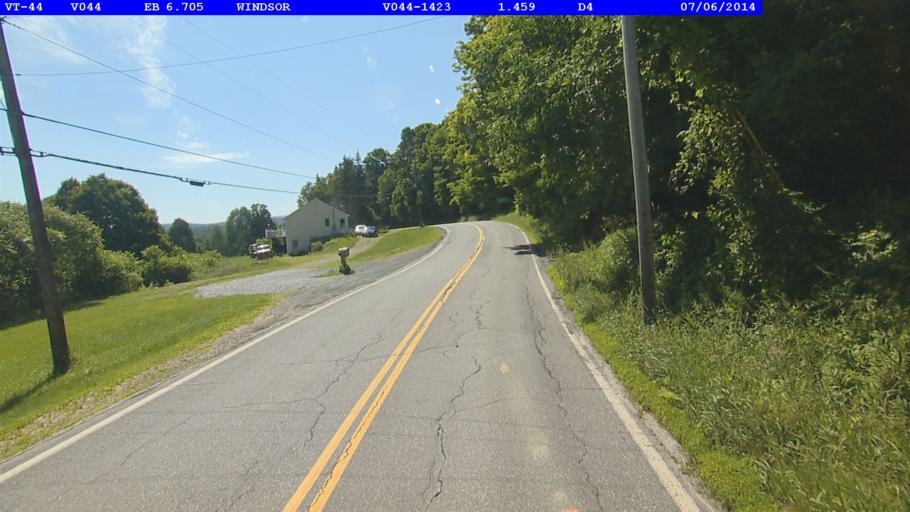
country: US
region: Vermont
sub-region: Windsor County
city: Windsor
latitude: 43.4606
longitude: -72.4266
